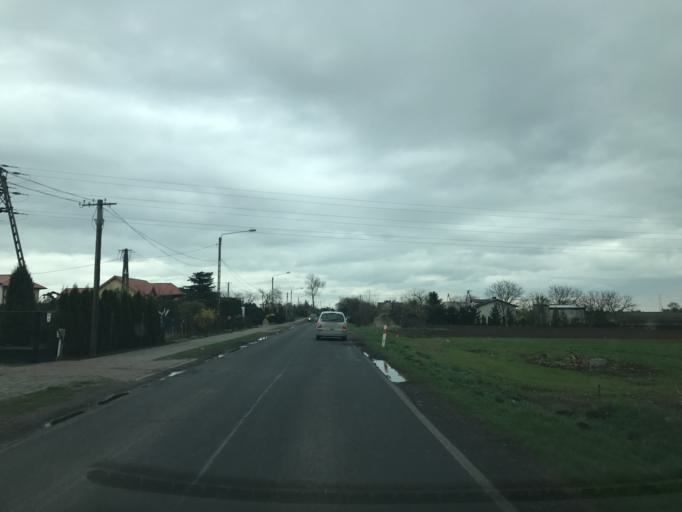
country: PL
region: Kujawsko-Pomorskie
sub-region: Powiat chelminski
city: Unislaw
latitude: 53.2063
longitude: 18.3984
